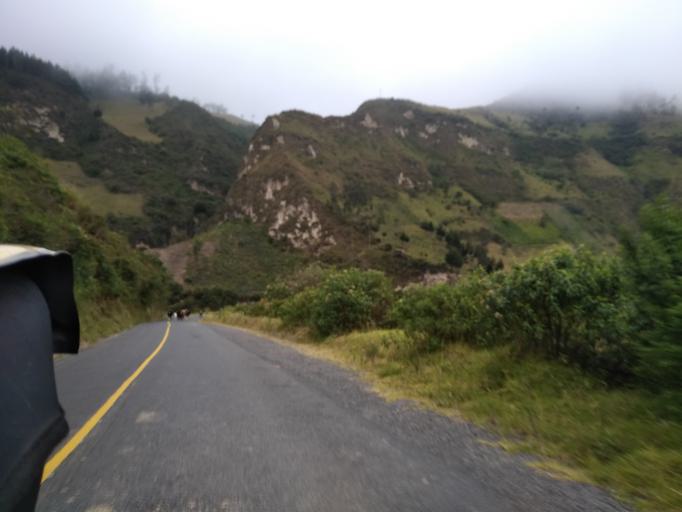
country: EC
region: Cotopaxi
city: Saquisili
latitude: -0.6860
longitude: -78.8666
